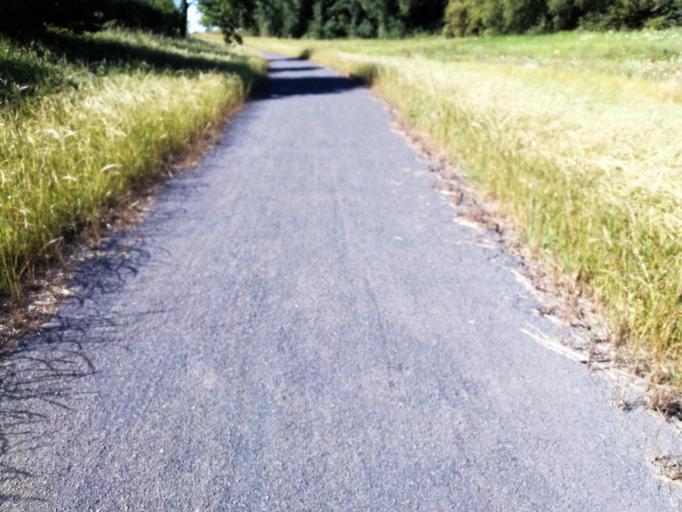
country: BE
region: Wallonia
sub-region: Province du Hainaut
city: Pecq
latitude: 50.7196
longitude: 3.3557
